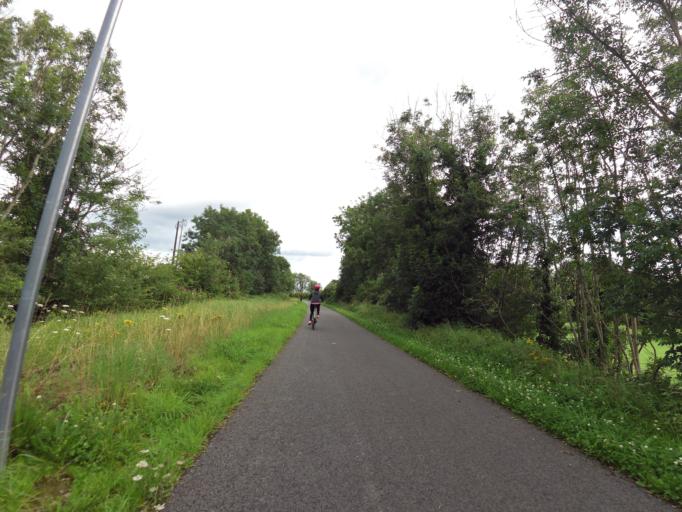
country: IE
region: Leinster
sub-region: An Iarmhi
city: An Muileann gCearr
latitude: 53.5102
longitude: -7.3827
